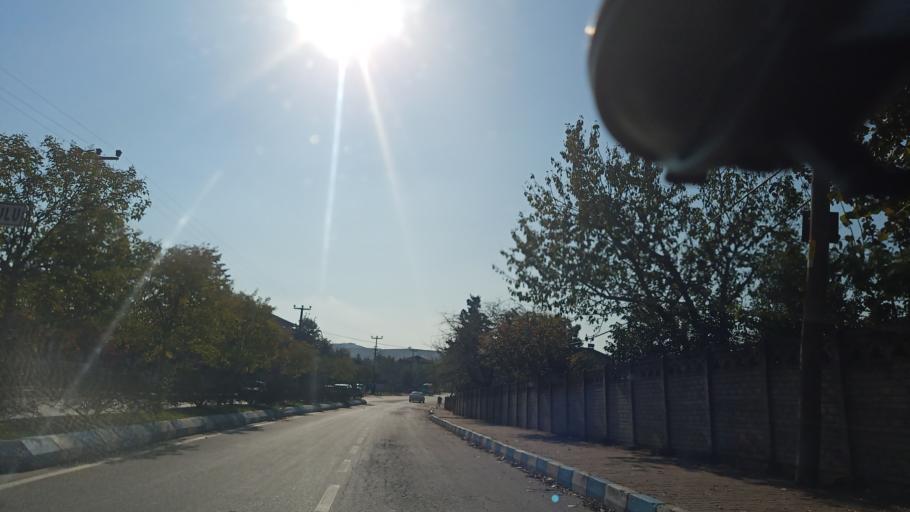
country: TR
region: Sakarya
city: Karasu
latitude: 41.0656
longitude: 30.8029
